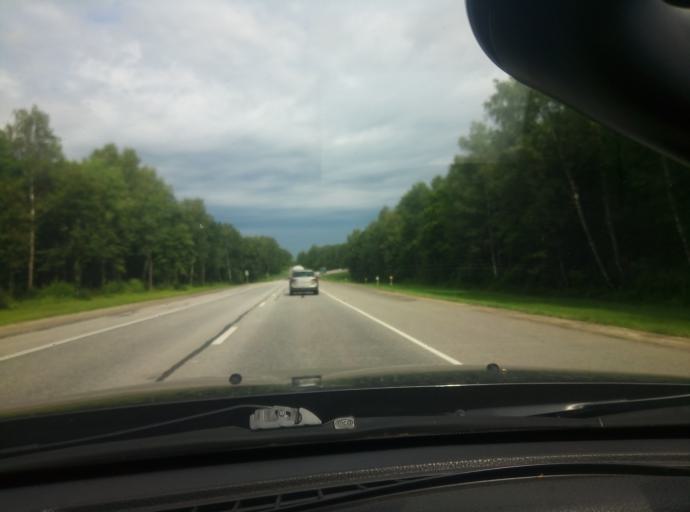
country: RU
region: Tula
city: Leninskiy
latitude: 54.3986
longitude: 37.5037
